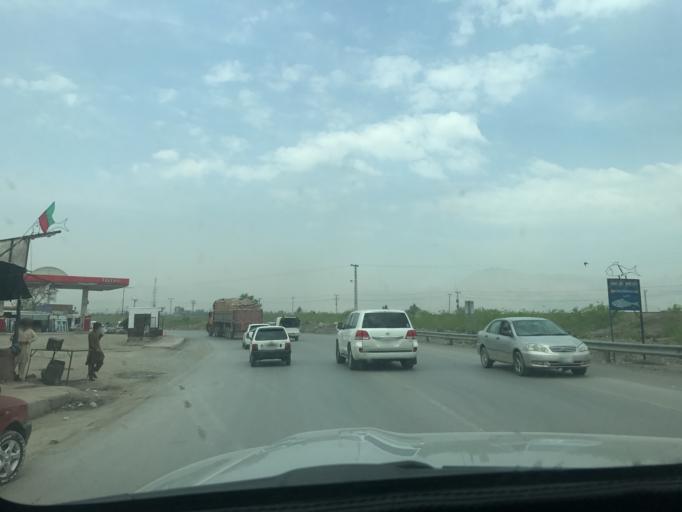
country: PK
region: Khyber Pakhtunkhwa
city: Peshawar
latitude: 34.0016
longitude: 71.3975
